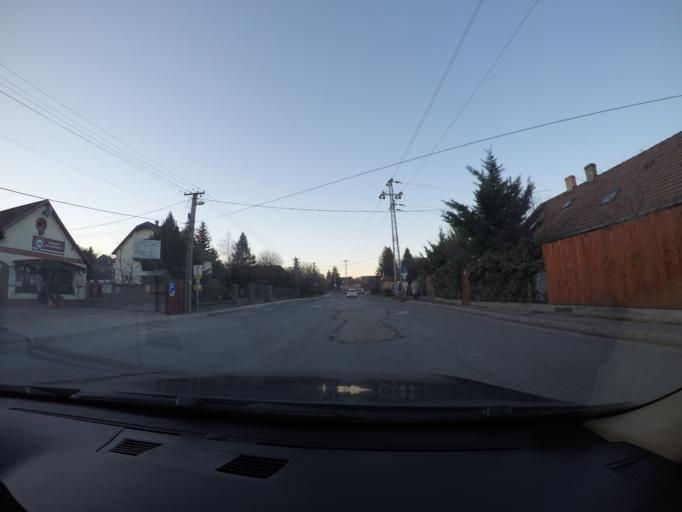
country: HU
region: Pest
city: Szentendre
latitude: 47.6739
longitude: 19.0717
